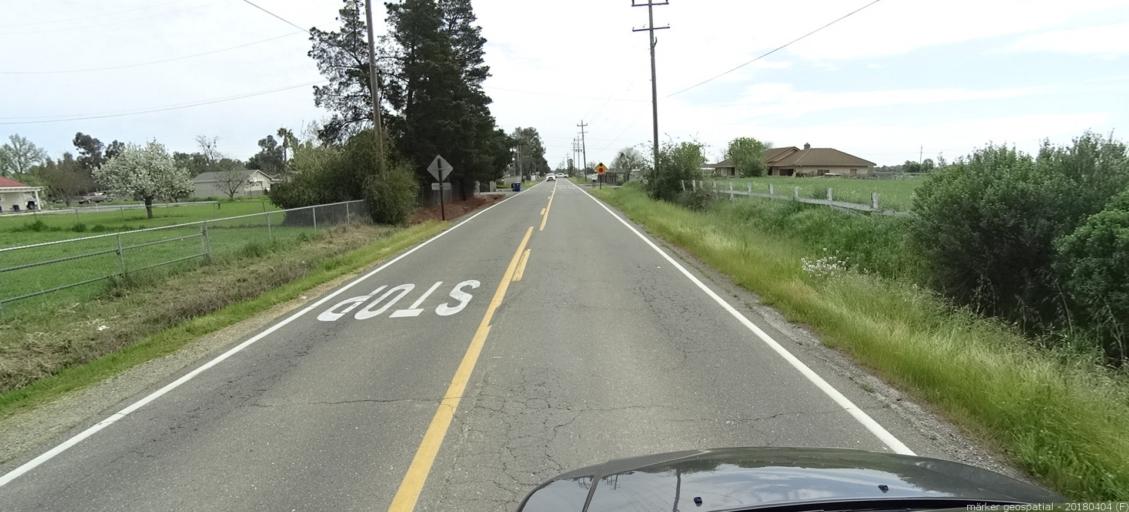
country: US
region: California
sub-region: Sacramento County
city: Galt
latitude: 38.2622
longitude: -121.2850
